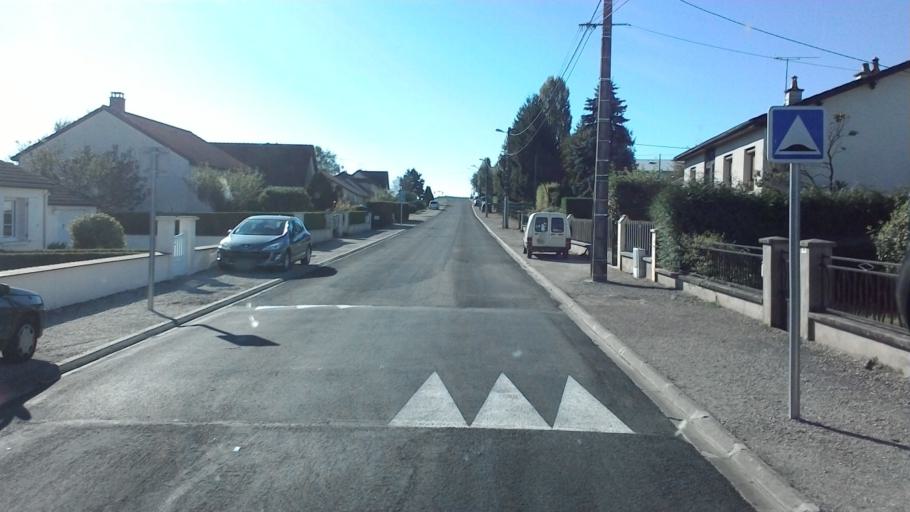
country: FR
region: Champagne-Ardenne
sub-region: Departement de la Haute-Marne
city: Chateauvillain
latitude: 48.0295
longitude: 4.9149
